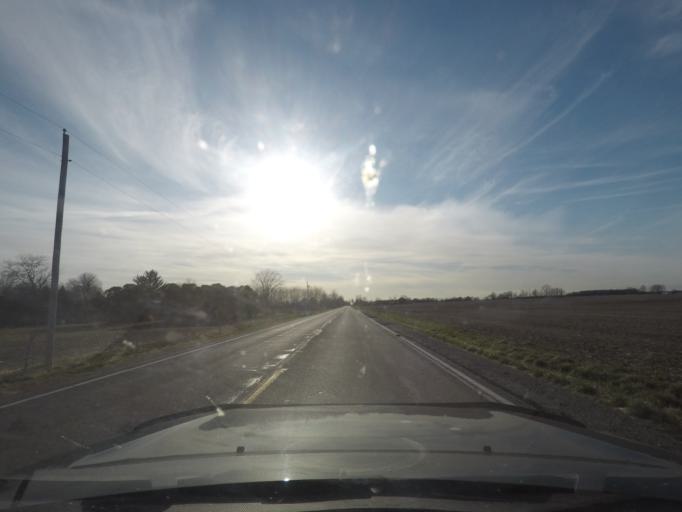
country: US
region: Indiana
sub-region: Saint Joseph County
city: Walkerton
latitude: 41.4483
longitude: -86.3983
